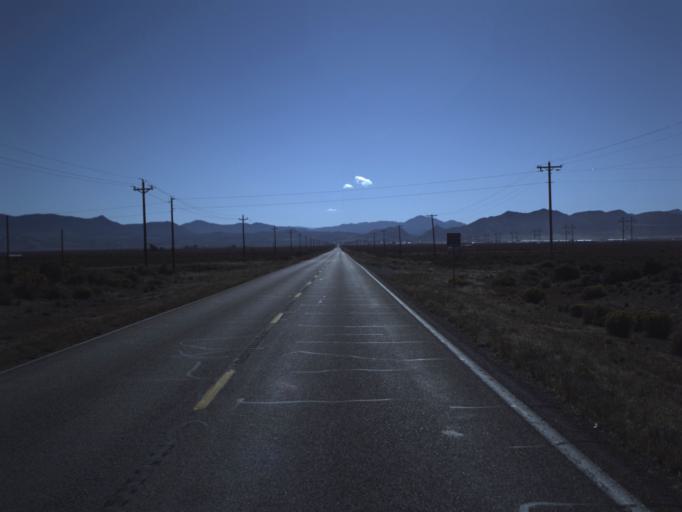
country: US
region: Utah
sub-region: Washington County
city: Enterprise
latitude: 37.7052
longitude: -113.6444
